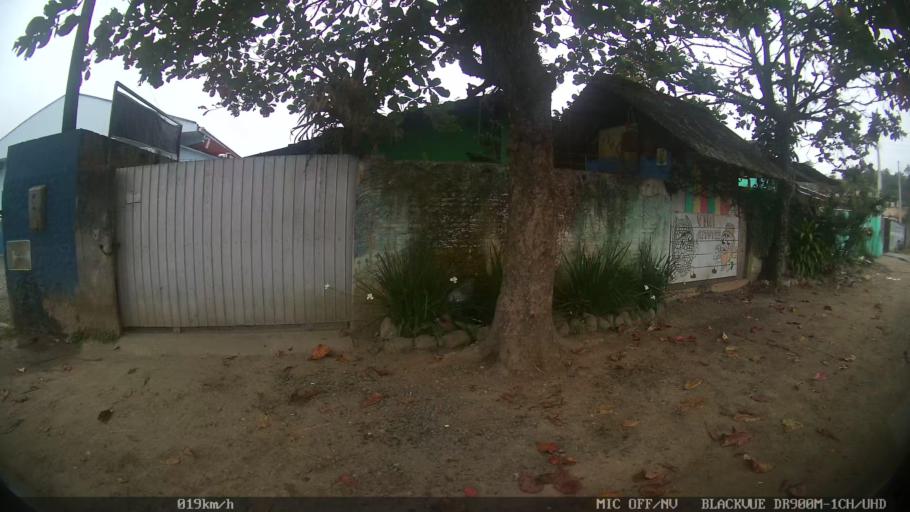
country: BR
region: Santa Catarina
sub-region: Joinville
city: Joinville
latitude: -26.2157
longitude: -48.8214
